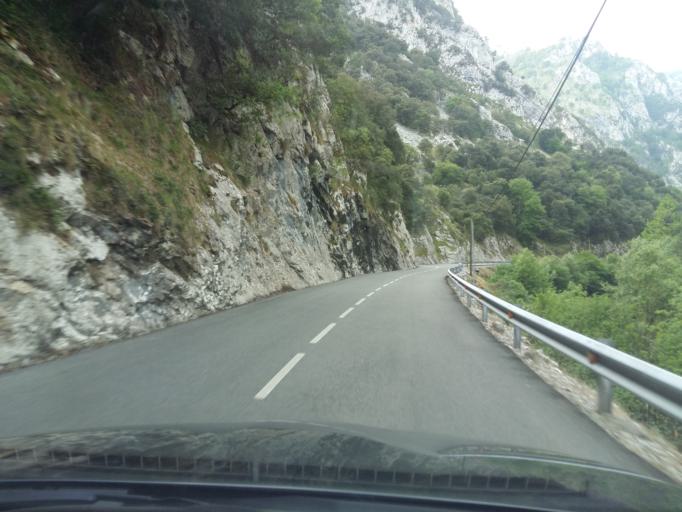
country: ES
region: Cantabria
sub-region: Provincia de Cantabria
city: Tresviso
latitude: 43.3052
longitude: -4.6051
